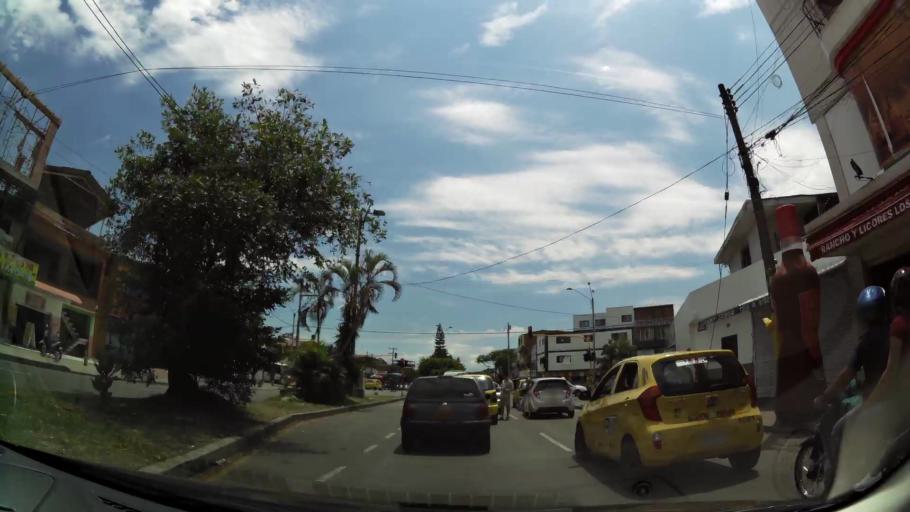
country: CO
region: Valle del Cauca
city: Cali
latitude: 3.4448
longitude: -76.5031
